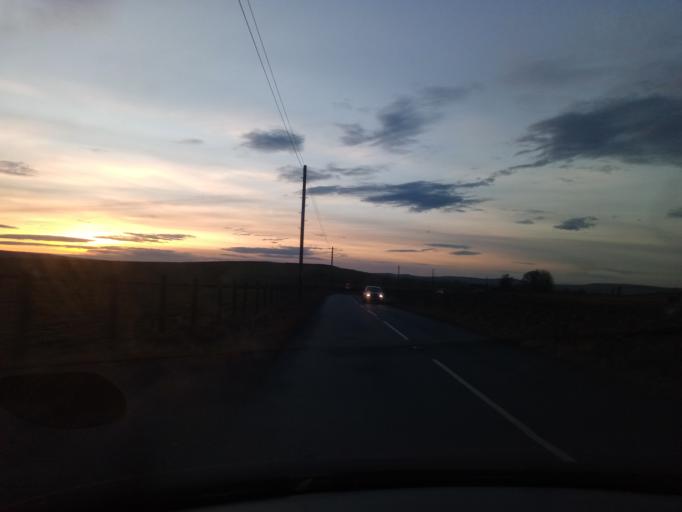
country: GB
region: England
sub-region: Northumberland
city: Otterburn
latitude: 55.2287
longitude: -2.1566
